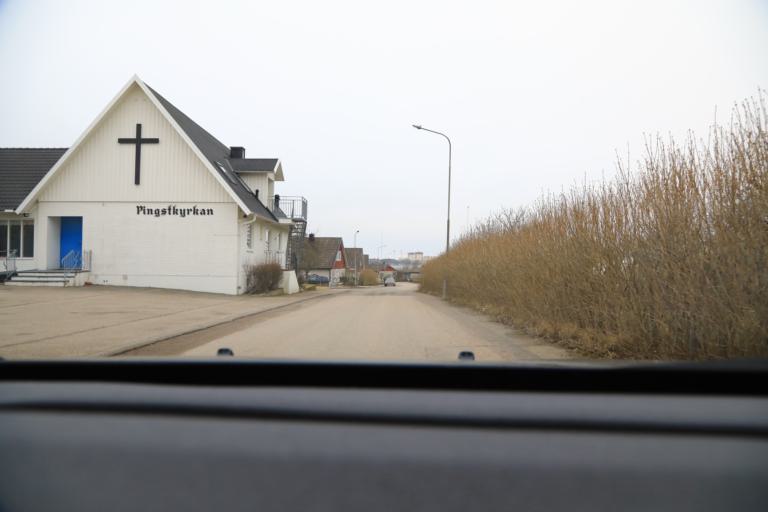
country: SE
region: Halland
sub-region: Kungsbacka Kommun
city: Frillesas
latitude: 57.2374
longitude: 12.1224
